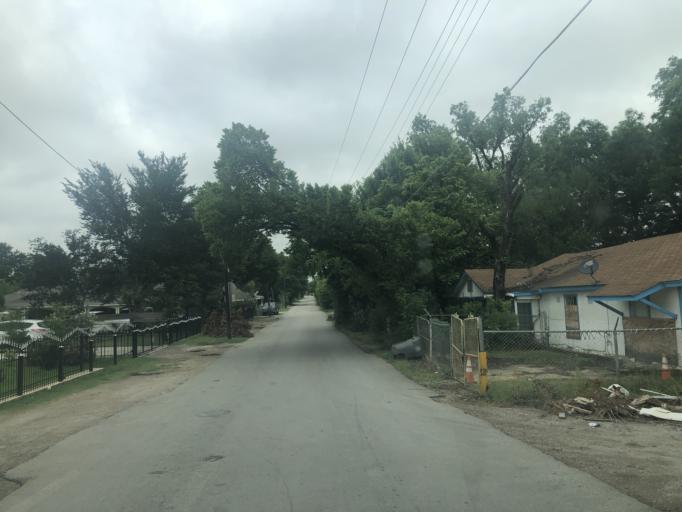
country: US
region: Texas
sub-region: Dallas County
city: Dallas
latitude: 32.7741
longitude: -96.8479
